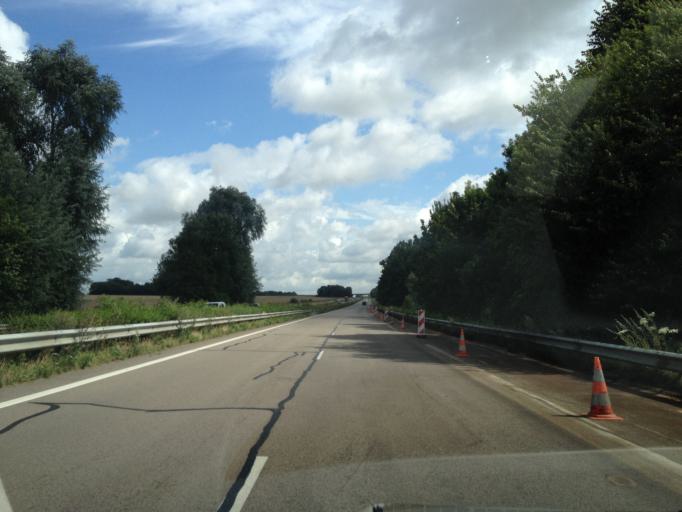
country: FR
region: Haute-Normandie
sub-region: Departement de la Seine-Maritime
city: Quincampoix
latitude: 49.5457
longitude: 1.2418
